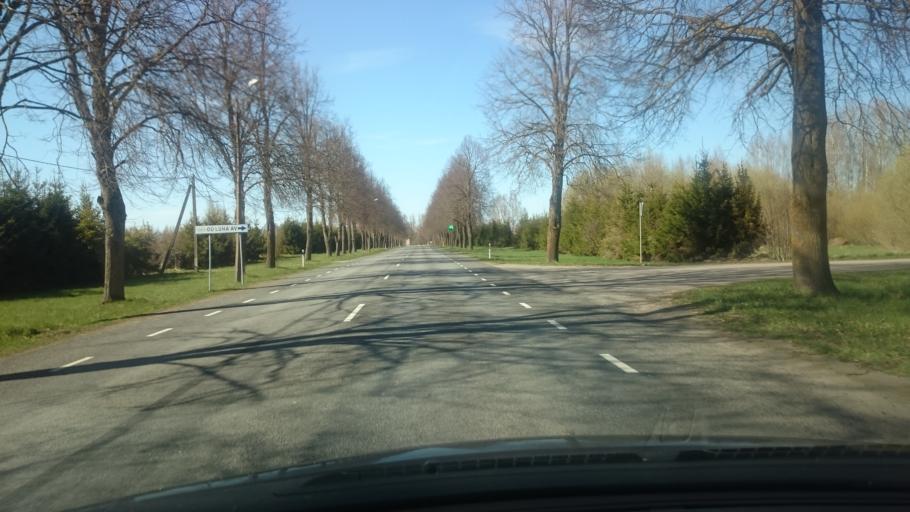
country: EE
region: Polvamaa
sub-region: Polva linn
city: Polva
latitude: 58.2015
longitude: 27.0768
